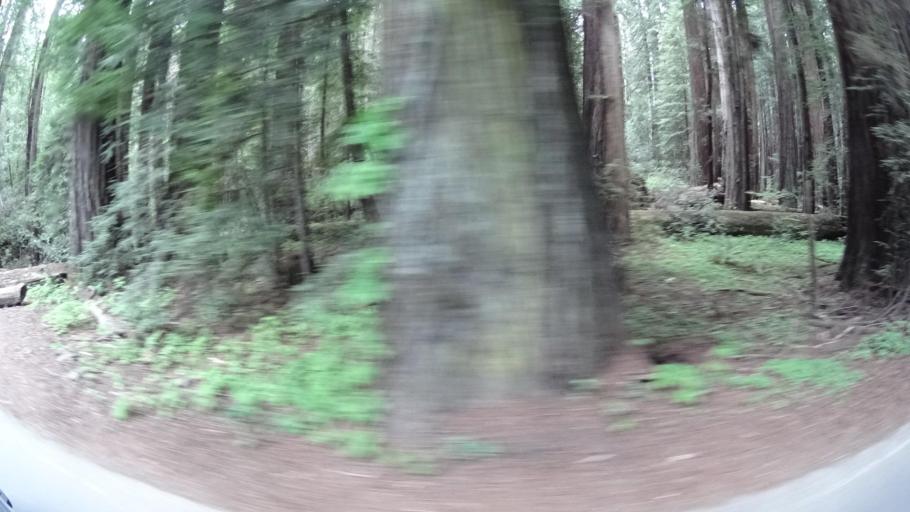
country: US
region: California
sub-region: Humboldt County
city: Redway
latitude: 40.1230
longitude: -123.8395
